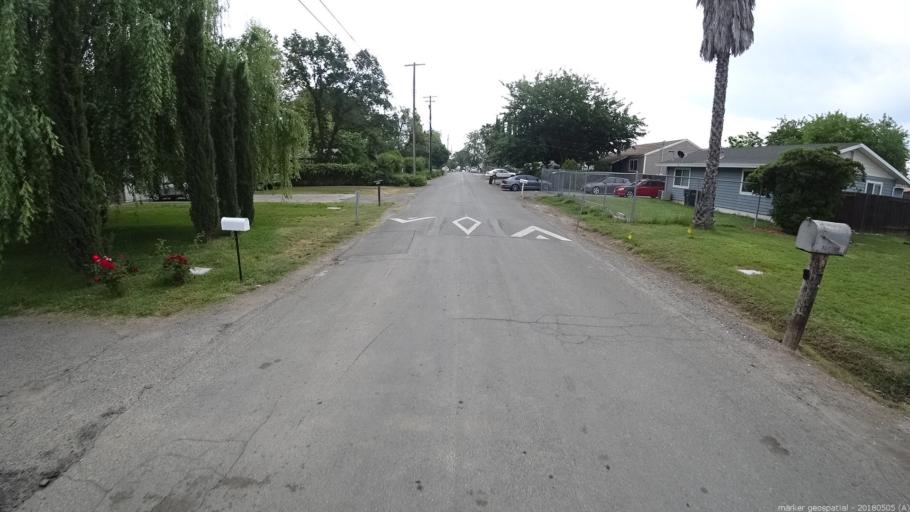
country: US
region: California
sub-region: Sacramento County
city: Rio Linda
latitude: 38.6638
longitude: -121.4420
